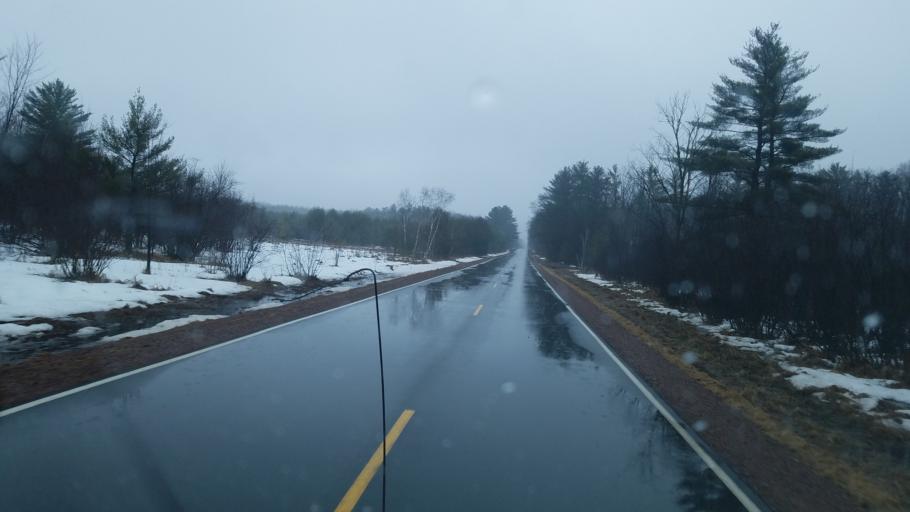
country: US
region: Wisconsin
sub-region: Wood County
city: Marshfield
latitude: 44.5330
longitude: -90.2997
